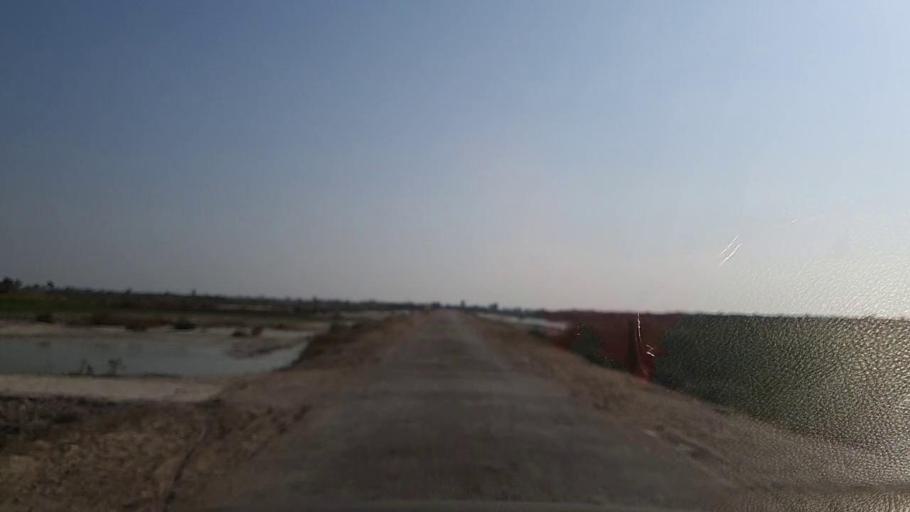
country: PK
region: Sindh
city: Sanghar
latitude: 26.0026
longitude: 69.0231
